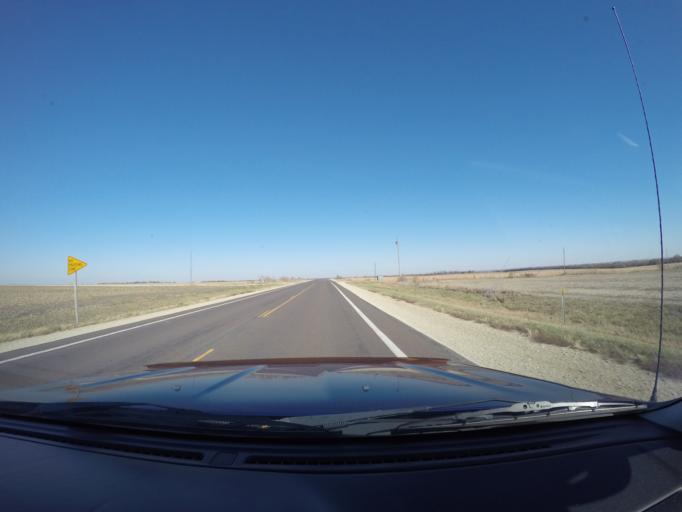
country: US
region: Kansas
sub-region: Marshall County
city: Blue Rapids
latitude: 39.6384
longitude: -96.7504
